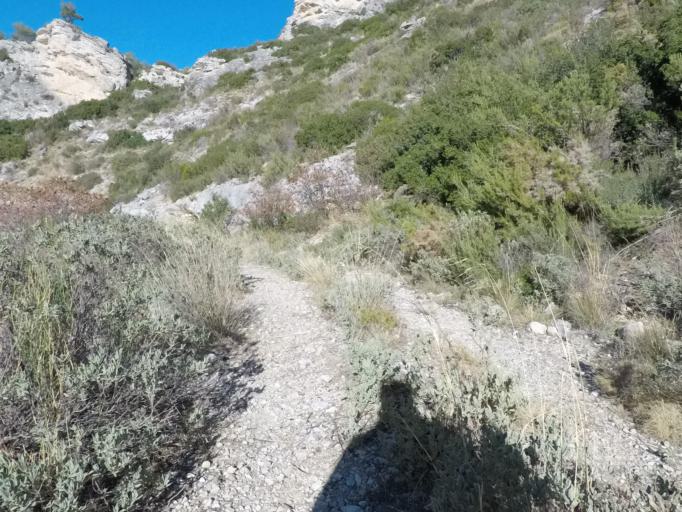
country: FR
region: Provence-Alpes-Cote d'Azur
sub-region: Departement des Bouches-du-Rhone
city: La Penne-sur-Huveaune
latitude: 43.2713
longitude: 5.4882
